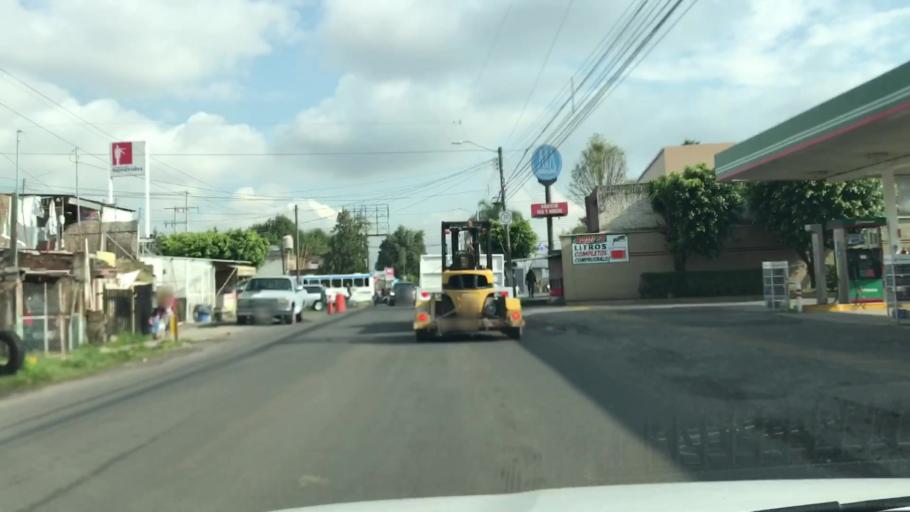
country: MX
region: Jalisco
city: Guadalajara
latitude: 20.6447
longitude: -103.4328
